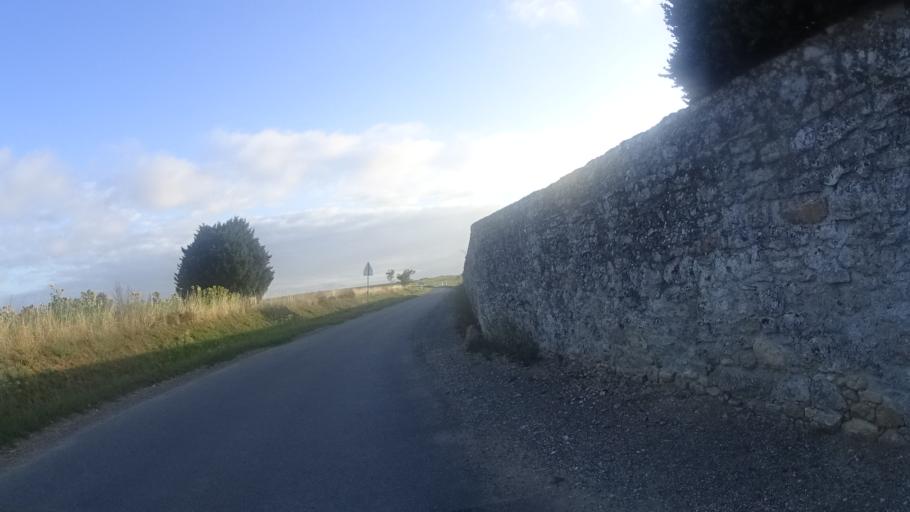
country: FR
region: Picardie
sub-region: Departement de l'Oise
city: Chamant
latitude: 49.1819
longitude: 2.6717
